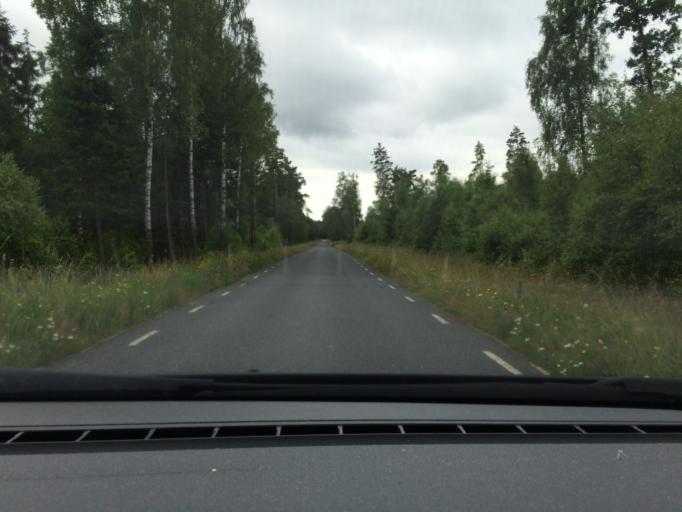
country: SE
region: Joenkoeping
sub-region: Varnamo Kommun
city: Forsheda
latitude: 57.0862
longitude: 13.8145
